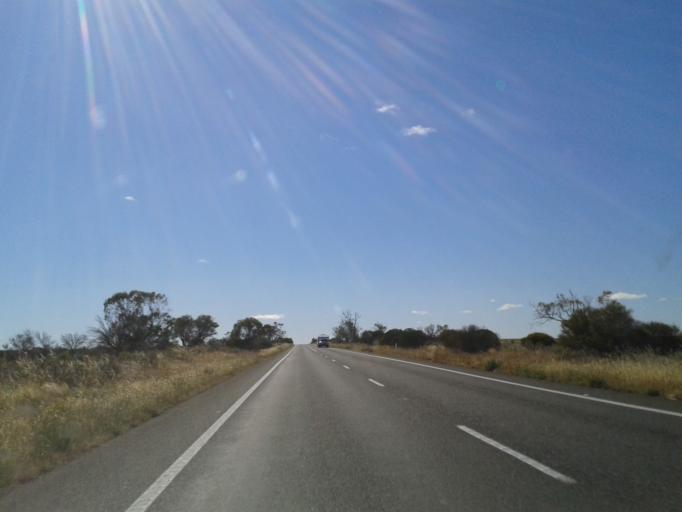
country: AU
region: South Australia
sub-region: Renmark Paringa
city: Renmark
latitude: -34.2750
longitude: 141.1063
